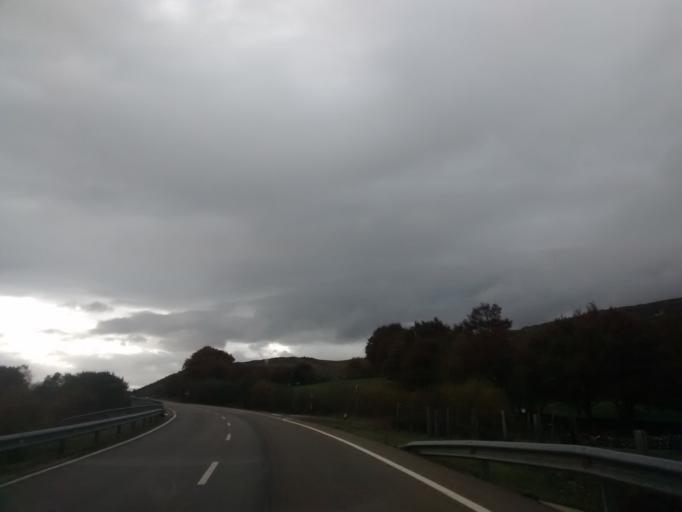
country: ES
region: Castille and Leon
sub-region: Provincia de Burgos
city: Arija
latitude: 43.0393
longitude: -3.9002
